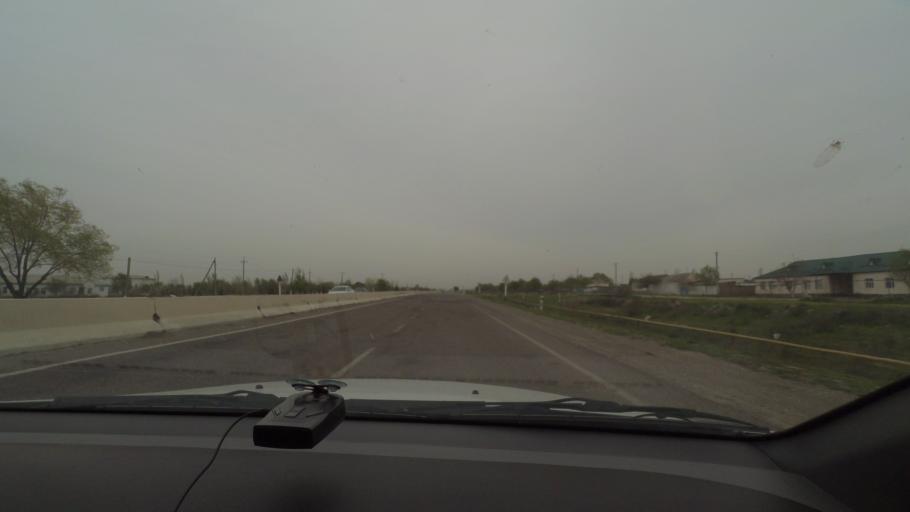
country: UZ
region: Sirdaryo
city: Guliston
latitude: 40.4924
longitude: 68.6868
